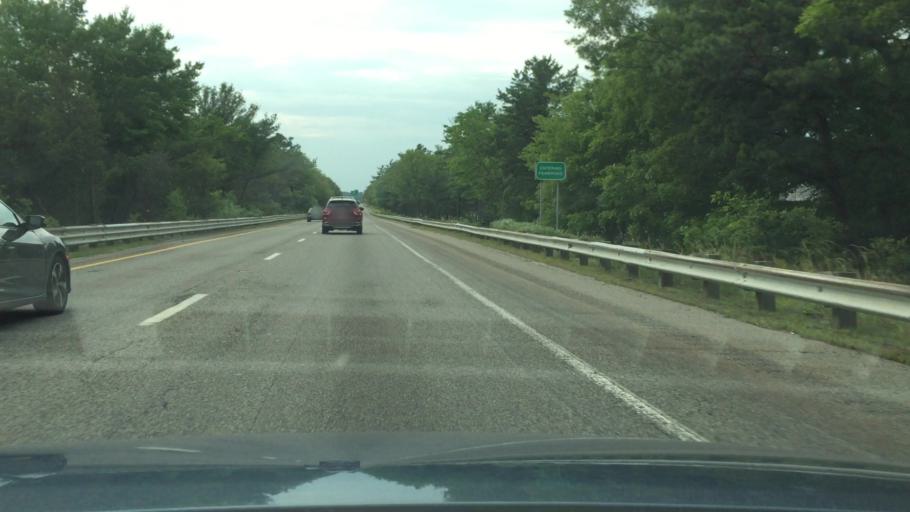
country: US
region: Massachusetts
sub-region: Plymouth County
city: North Pembroke
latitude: 42.1047
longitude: -70.7613
